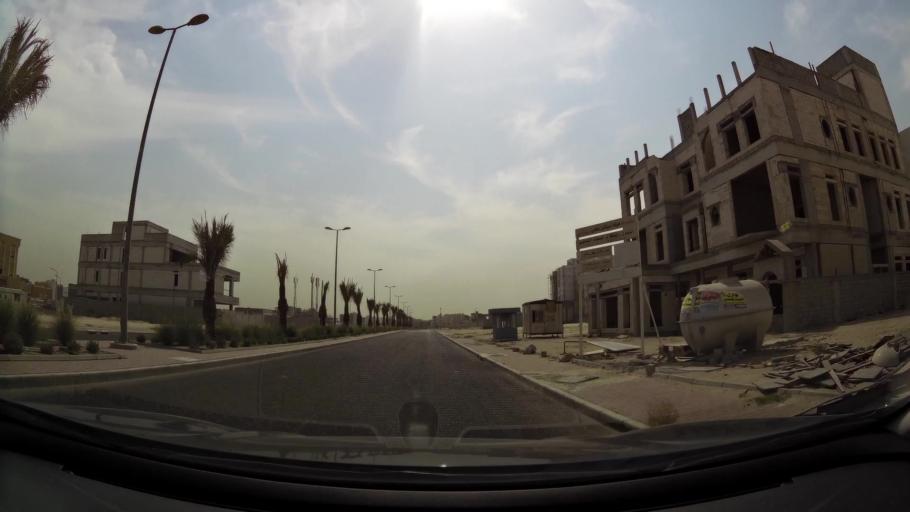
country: KW
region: Al Farwaniyah
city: Janub as Surrah
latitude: 29.2938
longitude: 47.9974
